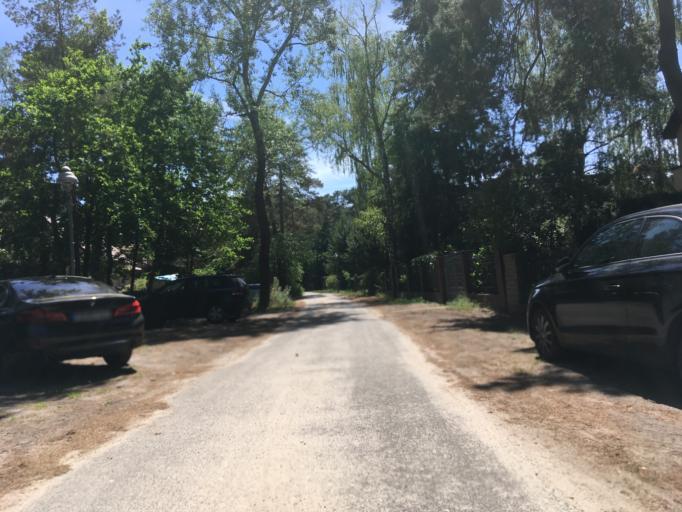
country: DE
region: Berlin
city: Schmockwitz
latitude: 52.3871
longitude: 13.6395
